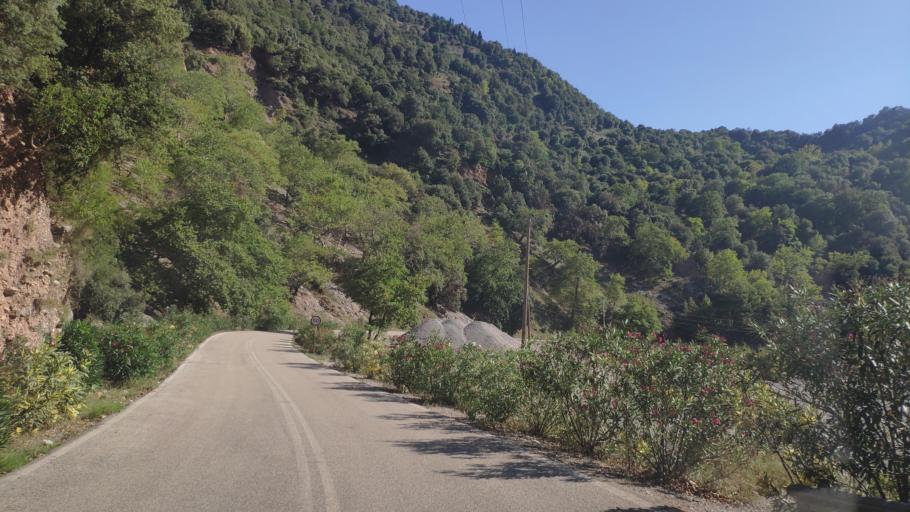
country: GR
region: Central Greece
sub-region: Nomos Evrytanias
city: Kerasochori
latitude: 39.0529
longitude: 21.6028
